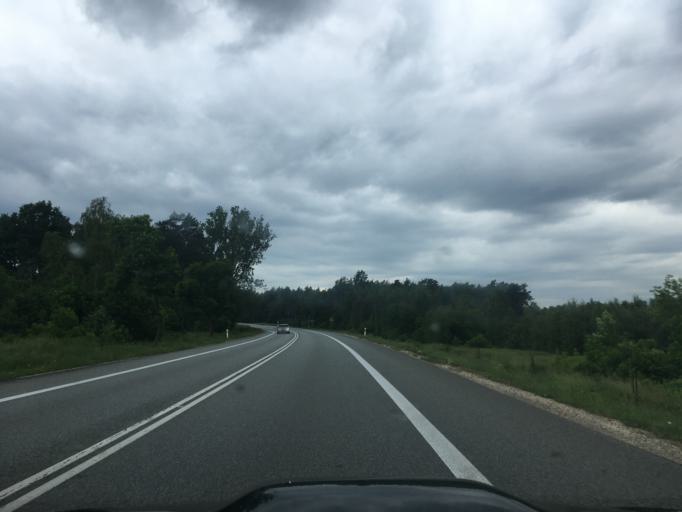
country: PL
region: Masovian Voivodeship
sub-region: Powiat otwocki
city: Celestynow
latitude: 52.0421
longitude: 21.3788
